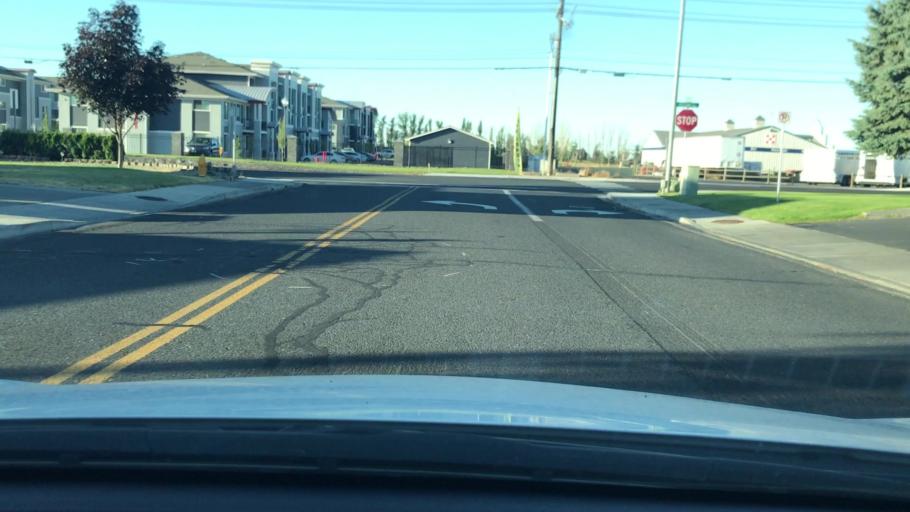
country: US
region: Washington
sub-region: Grant County
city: Moses Lake
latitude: 47.1168
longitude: -119.2554
